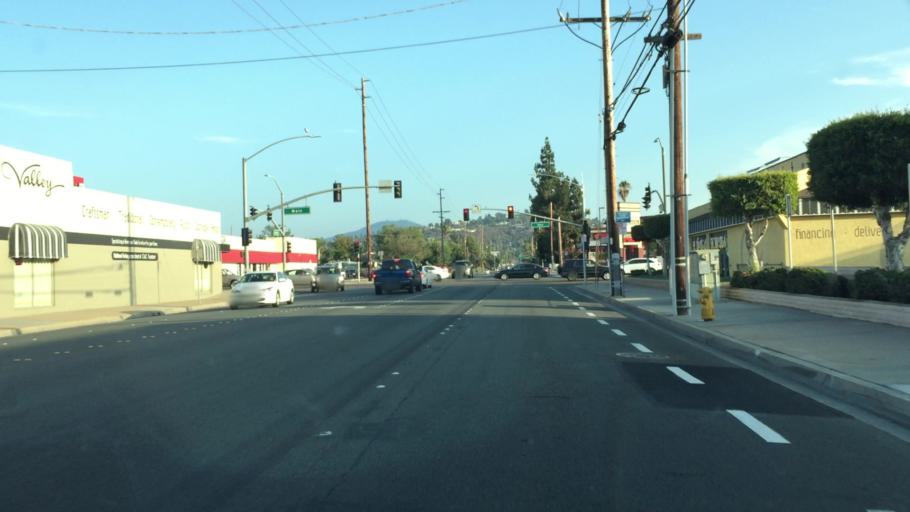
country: US
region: California
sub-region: San Diego County
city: El Cajon
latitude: 32.7956
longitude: -116.9511
